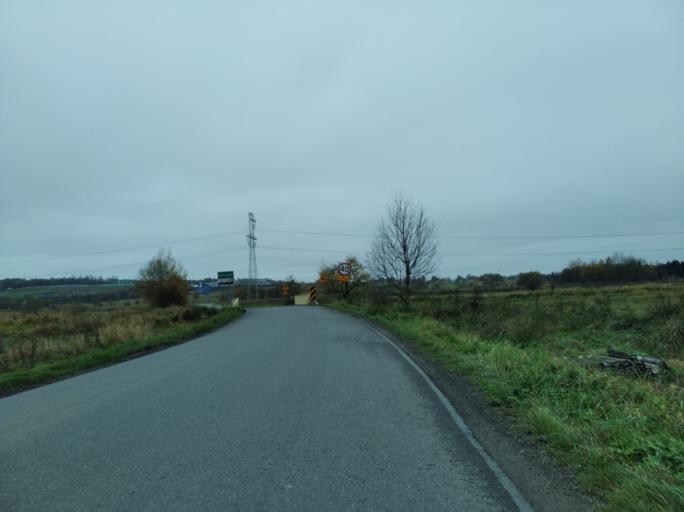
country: PL
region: Subcarpathian Voivodeship
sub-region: Powiat krosnienski
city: Odrzykon
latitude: 49.7214
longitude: 21.7620
